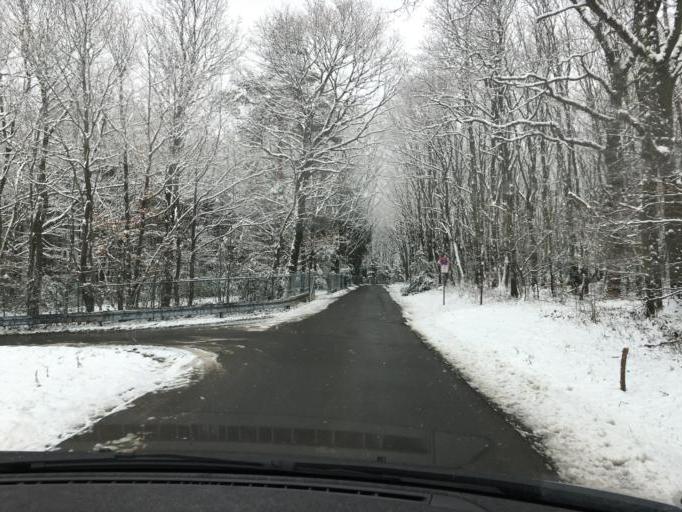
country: DE
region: North Rhine-Westphalia
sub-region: Regierungsbezirk Koln
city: Hurtgenwald
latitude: 50.7352
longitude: 6.4212
